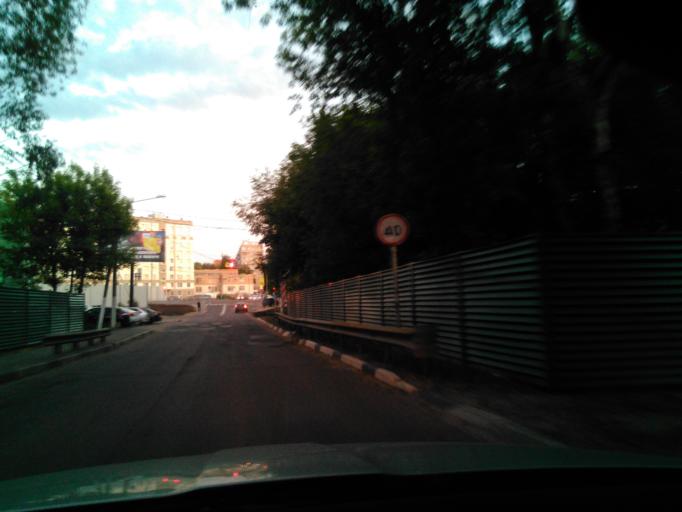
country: RU
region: Moskovskaya
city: Dolgoprudnyy
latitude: 55.9497
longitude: 37.5059
